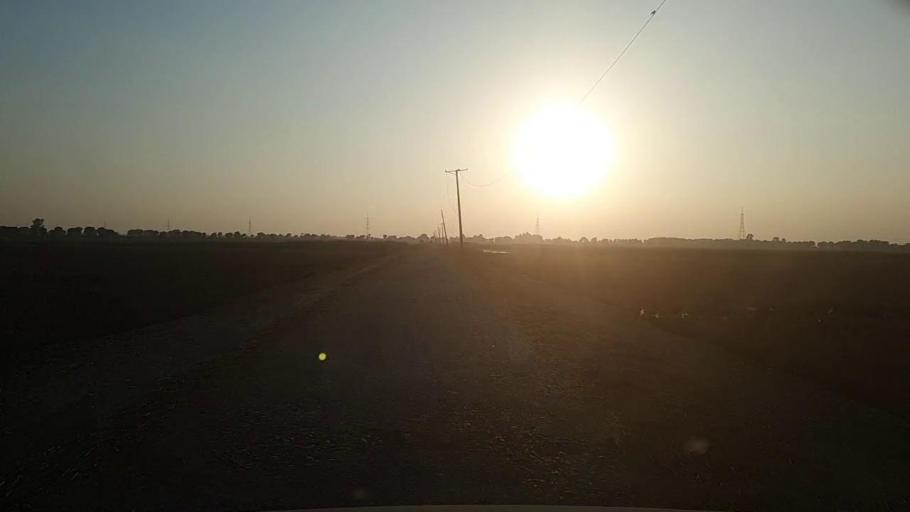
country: PK
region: Sindh
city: Mehar
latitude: 27.1931
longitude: 67.7487
